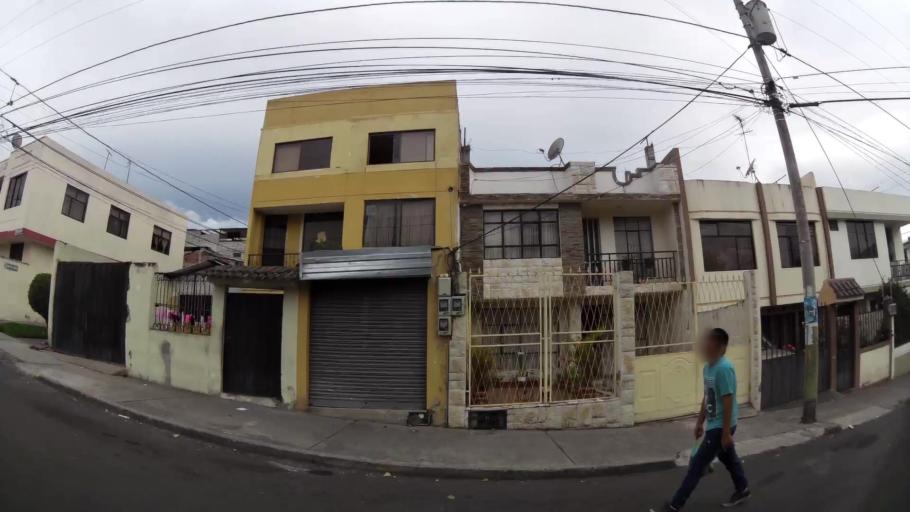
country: EC
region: Tungurahua
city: Ambato
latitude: -1.2618
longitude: -78.6337
